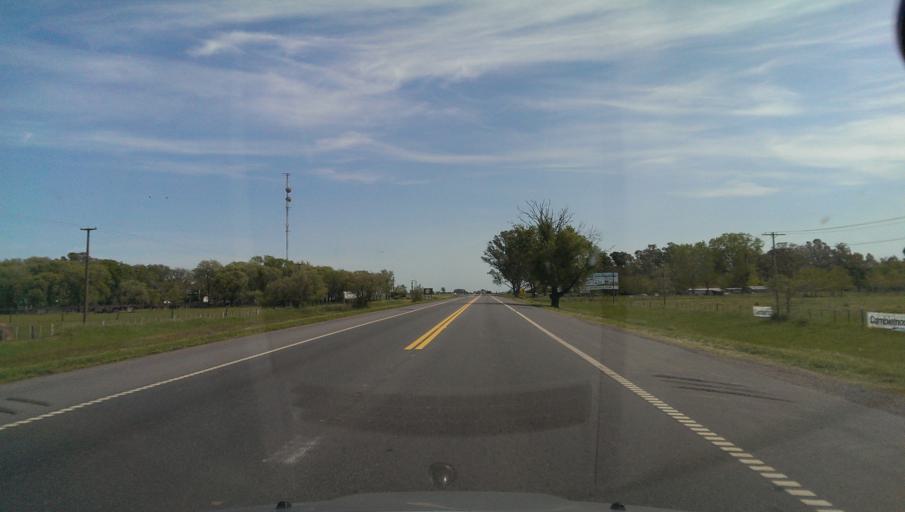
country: AR
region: Buenos Aires
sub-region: Partido de Azul
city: Azul
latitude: -36.3911
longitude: -59.4968
